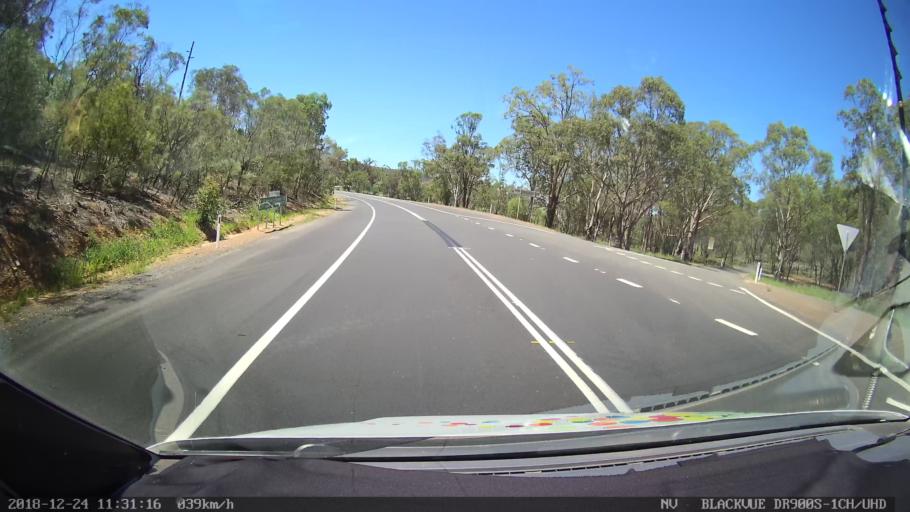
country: AU
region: New South Wales
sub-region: Upper Hunter Shire
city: Merriwa
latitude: -32.2129
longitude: 150.4608
